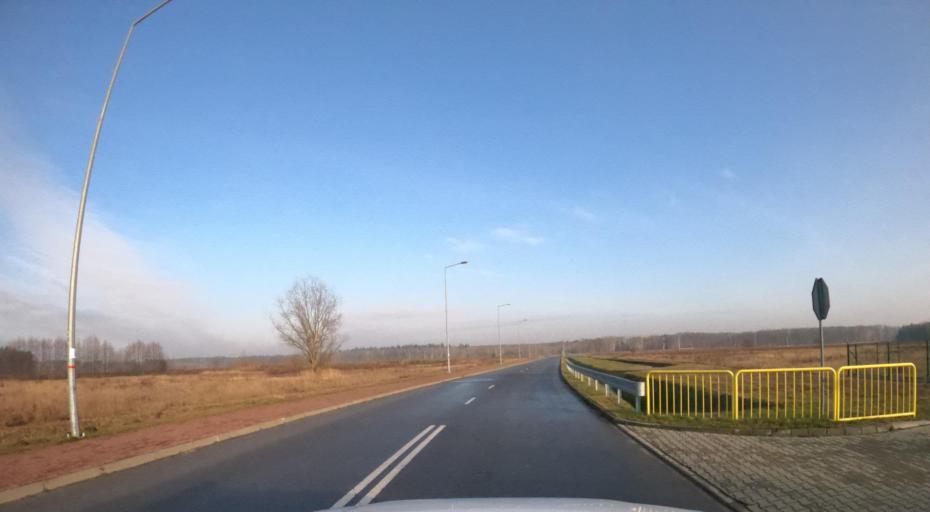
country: PL
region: Lubusz
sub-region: Powiat gorzowski
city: Kostrzyn nad Odra
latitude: 52.6264
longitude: 14.6109
